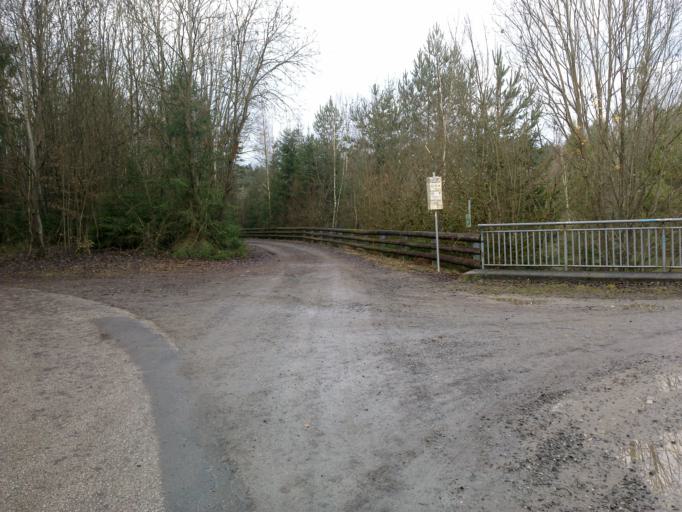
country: AT
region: Styria
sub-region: Politischer Bezirk Murtal
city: Weisskirchen in Steiermark
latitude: 47.1782
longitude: 14.7118
